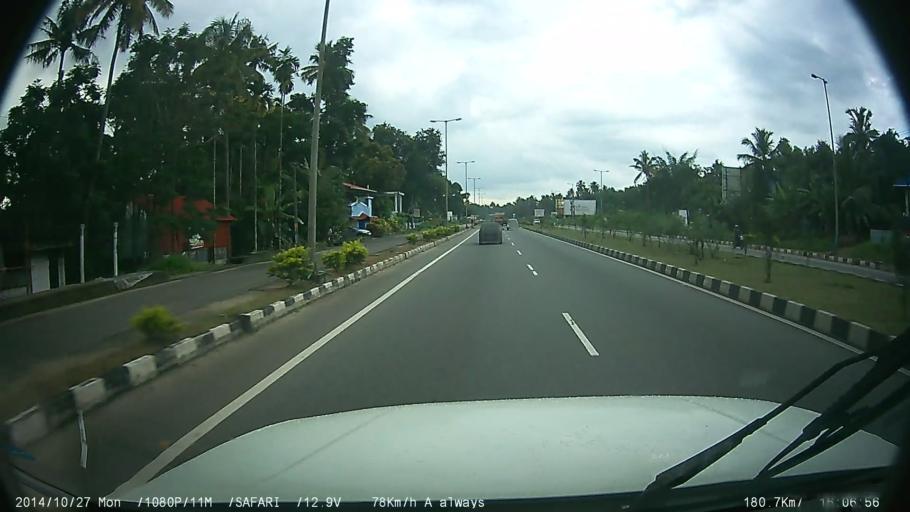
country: IN
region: Kerala
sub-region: Thrissur District
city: Kizhake Chalakudi
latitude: 10.3637
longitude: 76.3158
